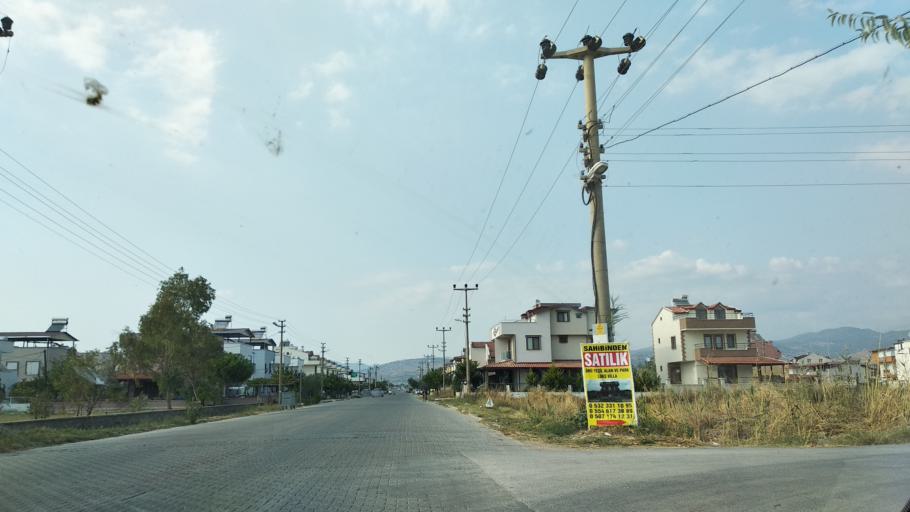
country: TR
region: Izmir
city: Dikili
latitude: 39.0998
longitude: 26.8828
